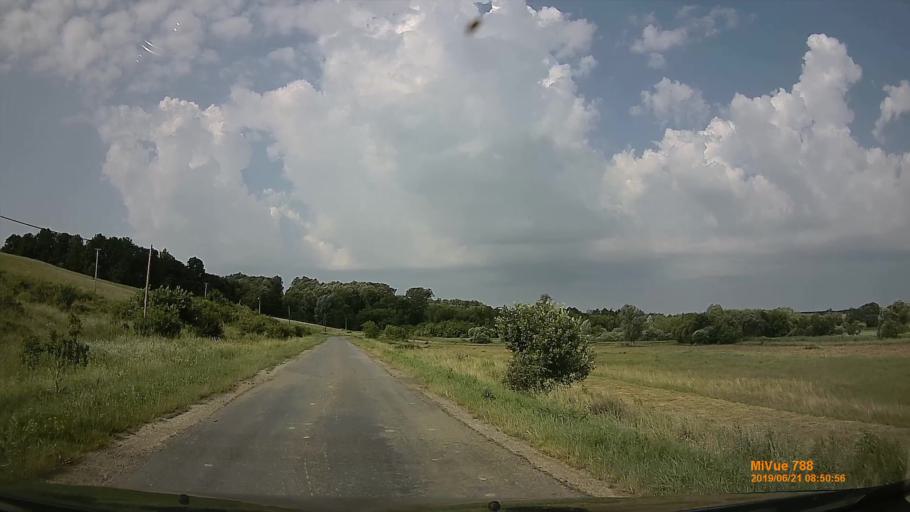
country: HU
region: Baranya
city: Buekkoesd
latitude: 46.1745
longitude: 17.9132
